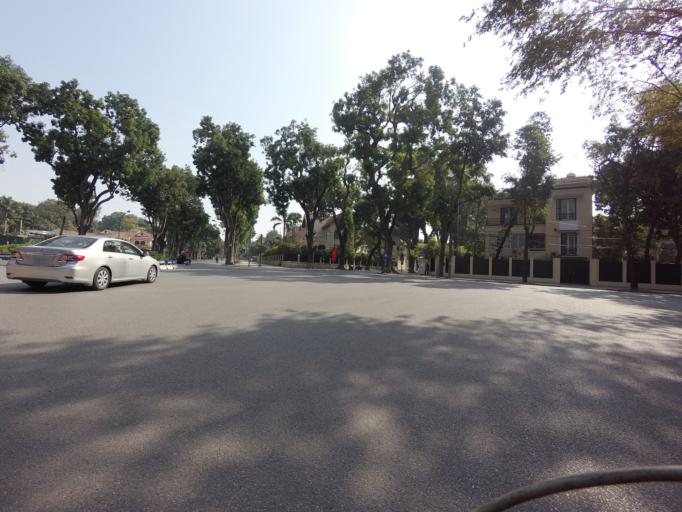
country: VN
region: Ha Noi
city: Hanoi
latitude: 21.0351
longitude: 105.8366
